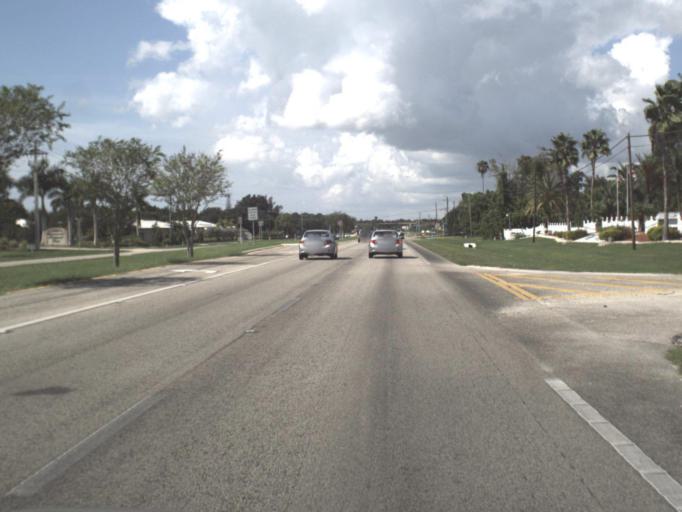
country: US
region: Florida
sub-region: Sarasota County
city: Osprey
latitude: 27.1872
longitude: -82.4859
